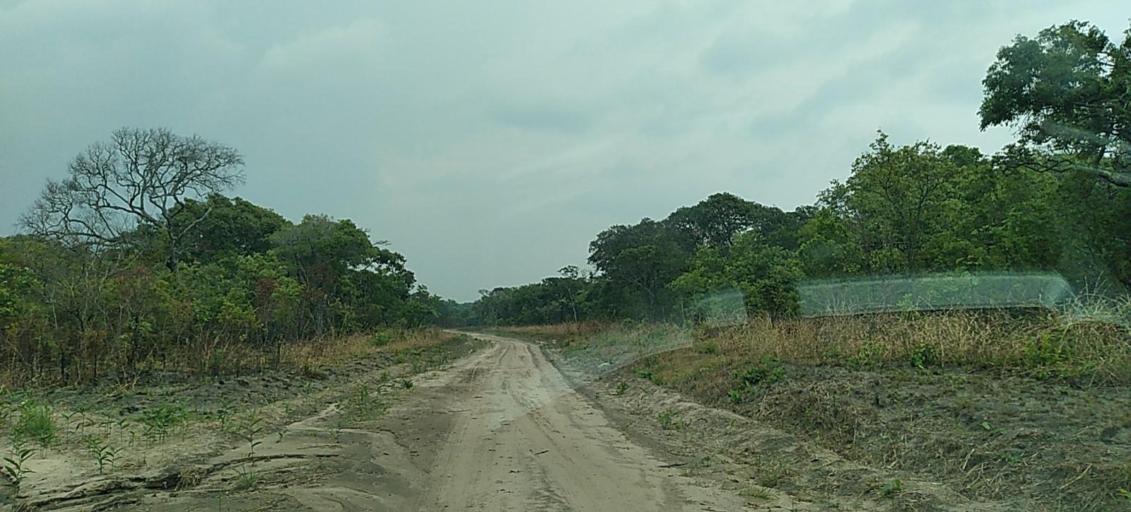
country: ZM
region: North-Western
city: Mwinilunga
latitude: -11.4235
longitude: 24.5939
